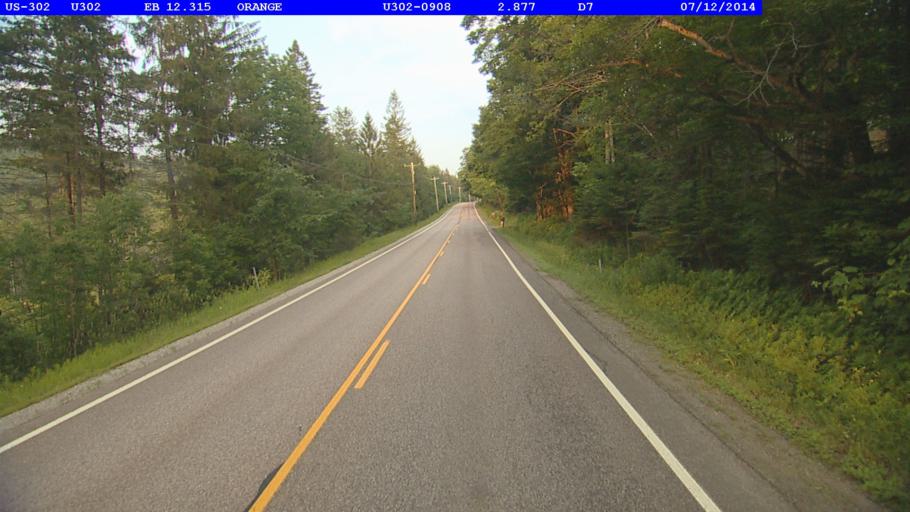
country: US
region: Vermont
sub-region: Washington County
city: South Barre
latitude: 44.1463
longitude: -72.3821
